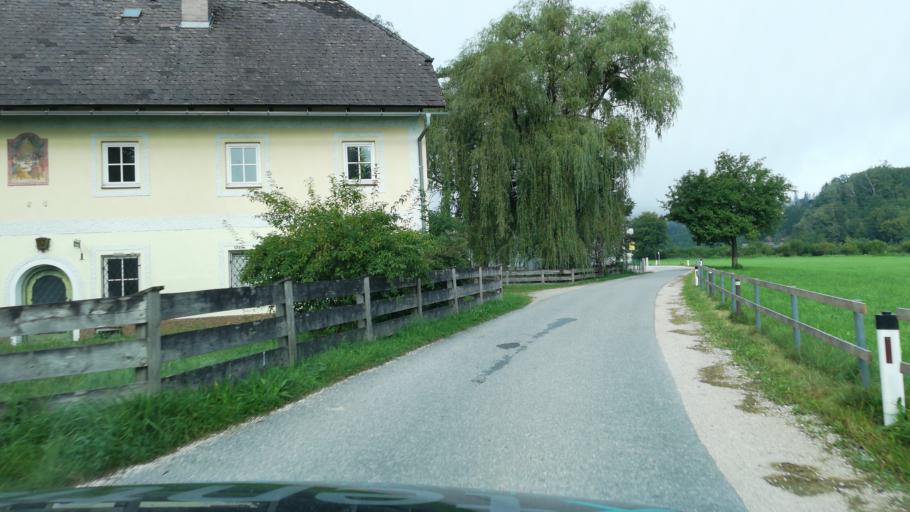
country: AT
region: Upper Austria
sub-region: Politischer Bezirk Steyr-Land
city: Maria Neustift
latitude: 47.8800
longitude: 14.5610
